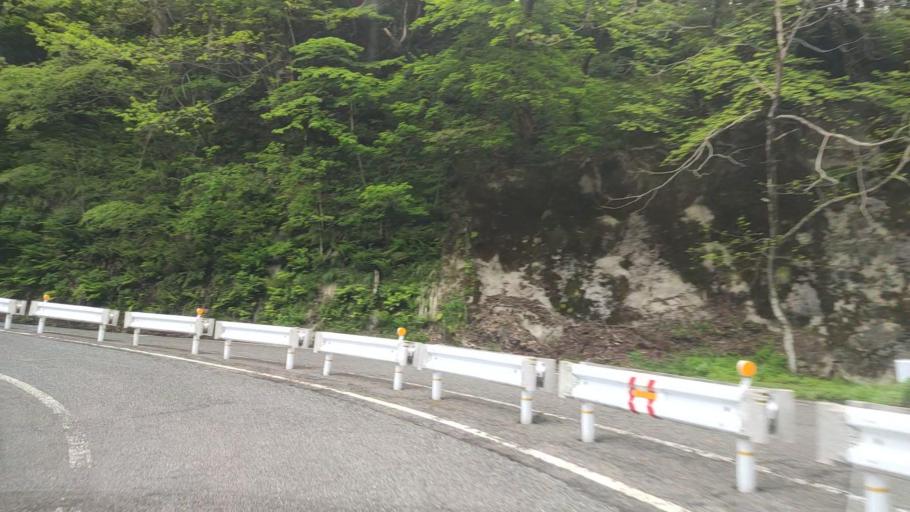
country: JP
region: Niigata
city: Gosen
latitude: 37.7163
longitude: 139.1143
